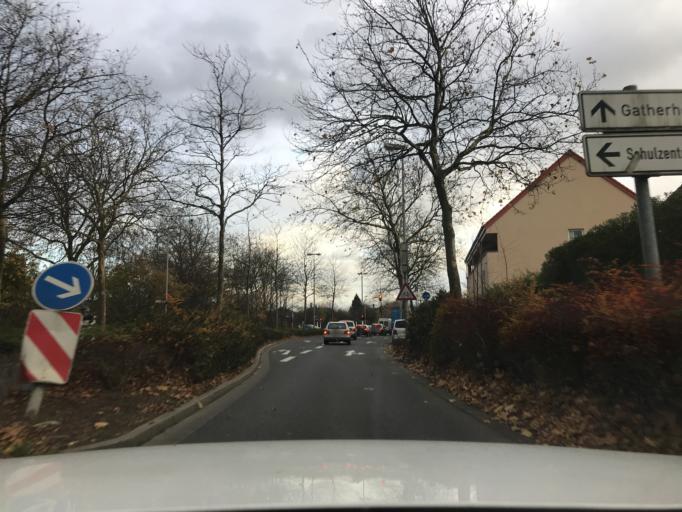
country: DE
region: North Rhine-Westphalia
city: Tonisvorst
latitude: 51.3305
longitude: 6.5269
